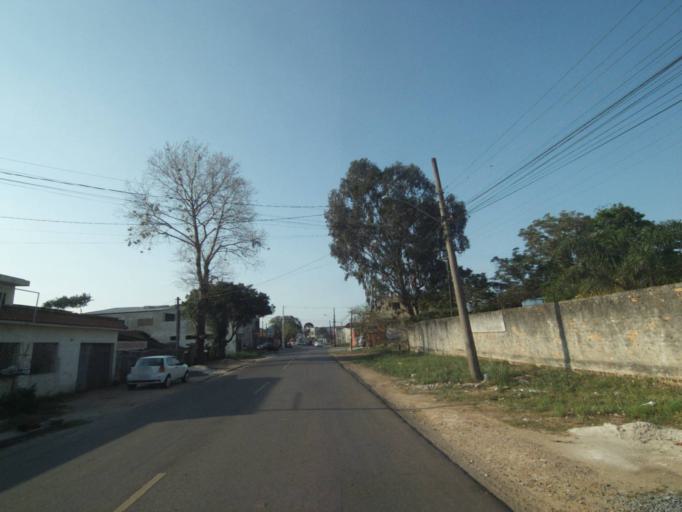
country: BR
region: Parana
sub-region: Curitiba
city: Curitiba
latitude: -25.4907
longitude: -49.3354
